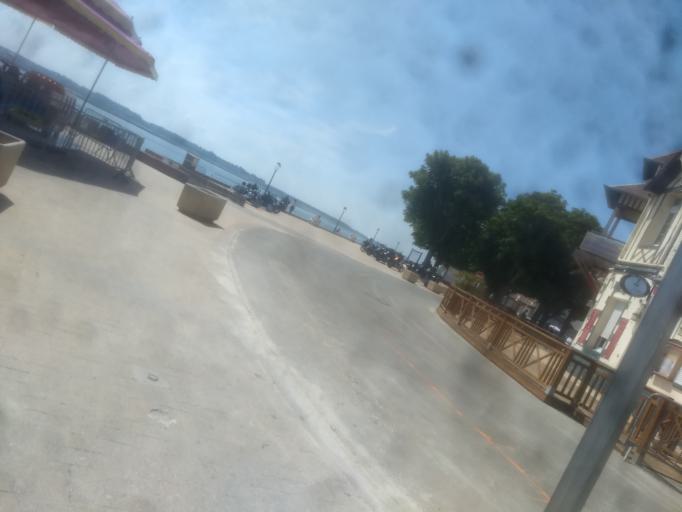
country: FR
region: Picardie
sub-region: Departement de la Somme
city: Le Crotoy
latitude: 50.2149
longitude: 1.6293
